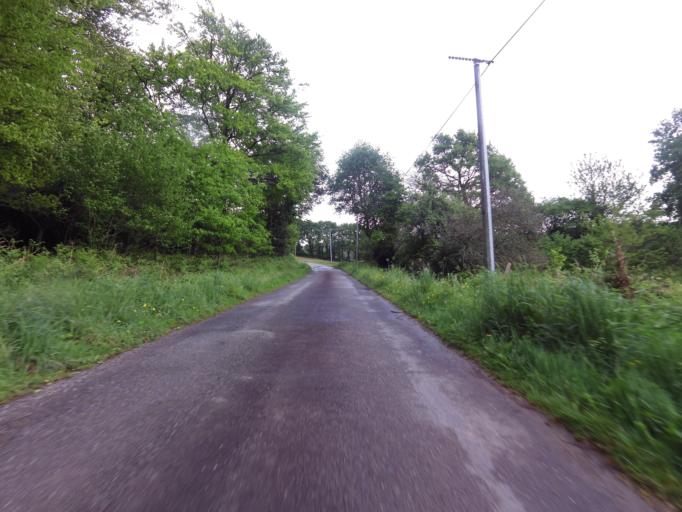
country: FR
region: Brittany
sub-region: Departement du Morbihan
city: Pluherlin
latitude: 47.7138
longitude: -2.3880
